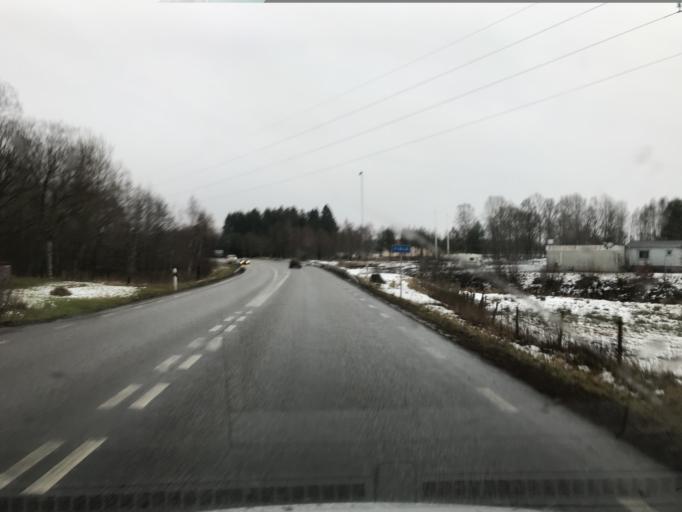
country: SE
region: Skane
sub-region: Hassleholms Kommun
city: Tormestorp
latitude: 56.1736
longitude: 13.6895
